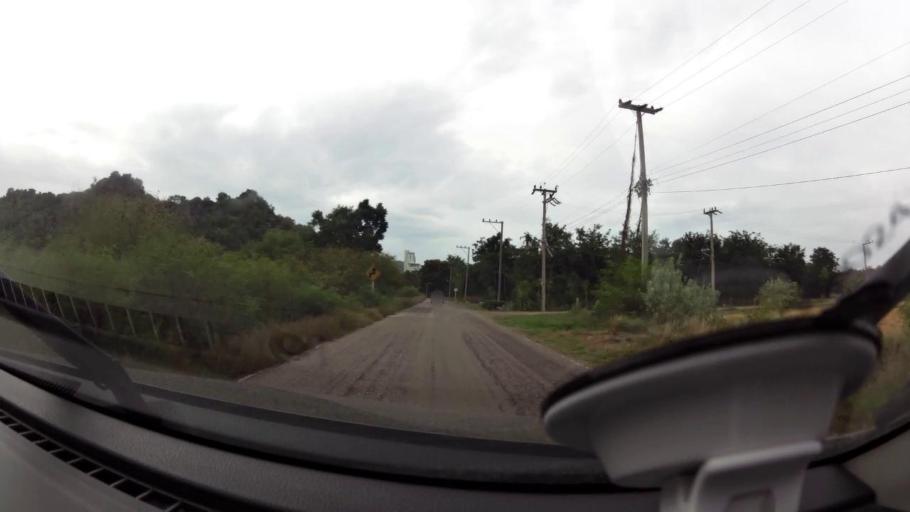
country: TH
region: Prachuap Khiri Khan
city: Pran Buri
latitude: 12.4239
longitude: 99.9793
